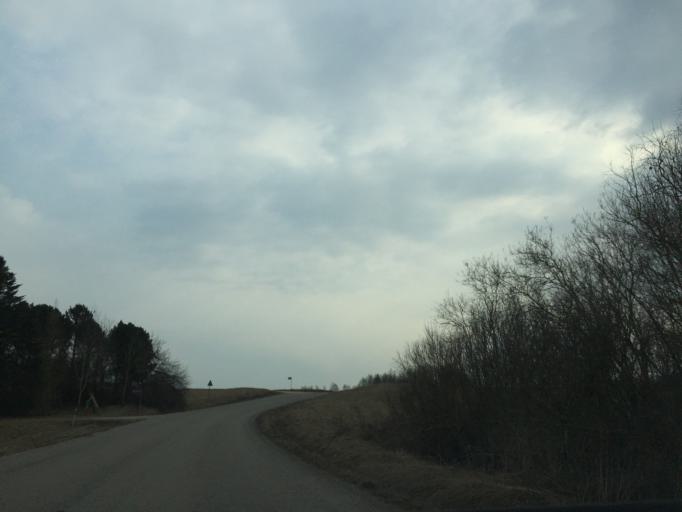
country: LV
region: Priekuli
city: Priekuli
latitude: 57.2331
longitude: 25.3809
